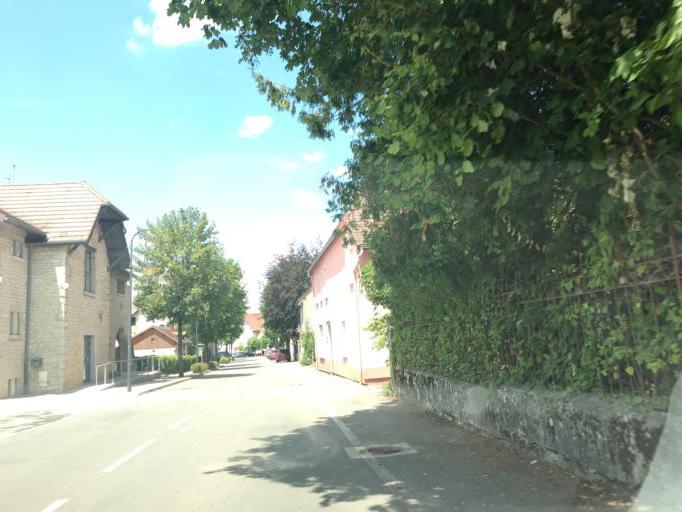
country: FR
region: Franche-Comte
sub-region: Departement du Jura
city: Clairvaux-les-Lacs
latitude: 46.5741
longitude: 5.7522
